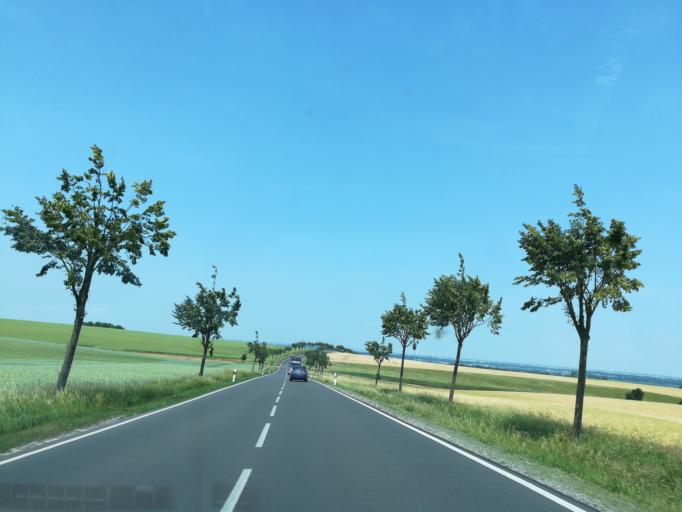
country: DE
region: Saxony-Anhalt
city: Schneidlingen
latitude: 51.8693
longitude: 11.4482
